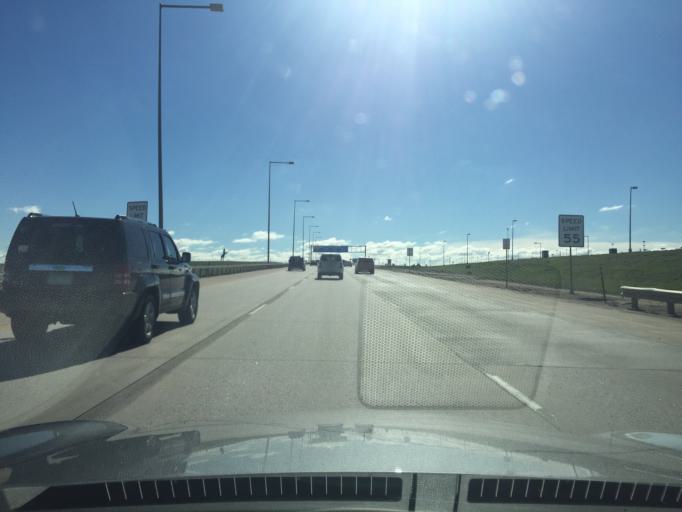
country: US
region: Colorado
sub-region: Weld County
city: Lochbuie
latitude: 39.8335
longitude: -104.6815
